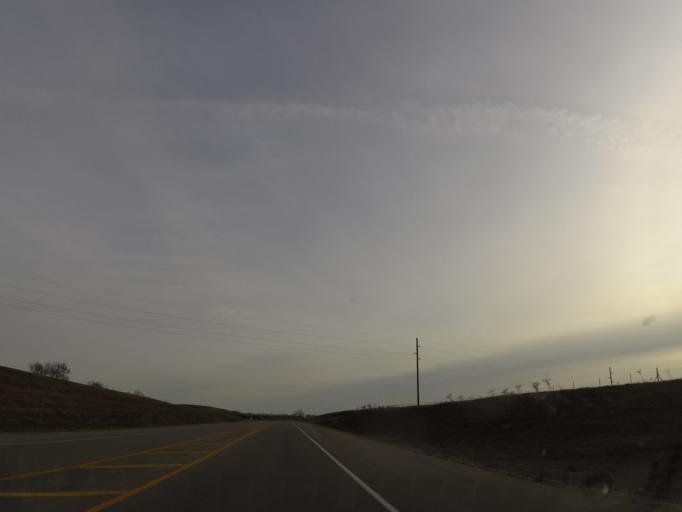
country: US
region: Kentucky
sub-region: Harrison County
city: Cynthiana
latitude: 38.3742
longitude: -84.3245
